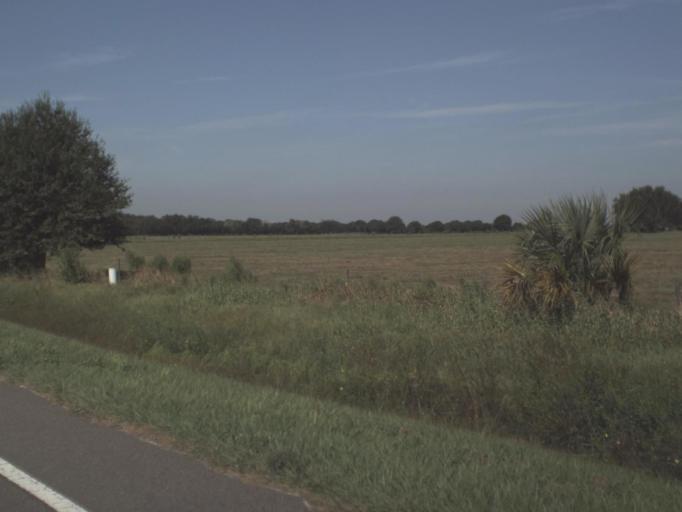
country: US
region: Florida
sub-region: Hardee County
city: Wauchula
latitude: 27.5515
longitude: -81.7381
